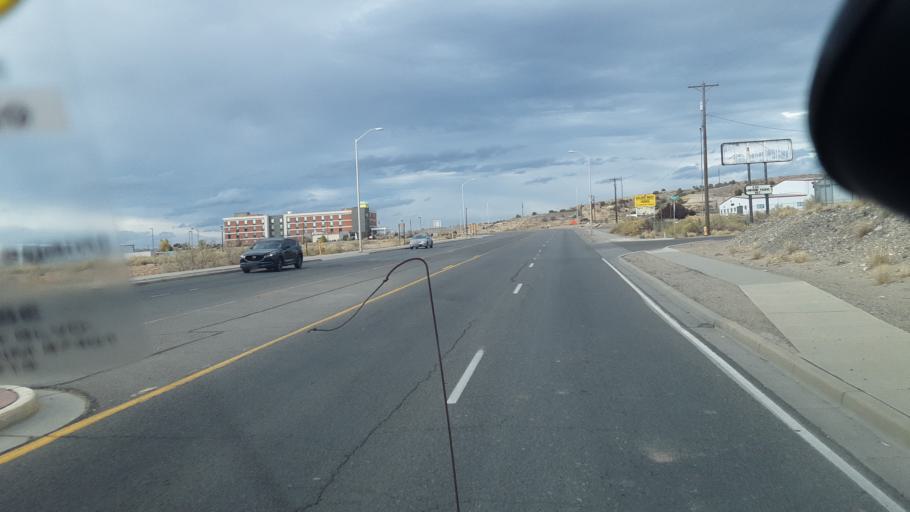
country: US
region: New Mexico
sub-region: San Juan County
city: Farmington
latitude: 36.7205
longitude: -108.1573
